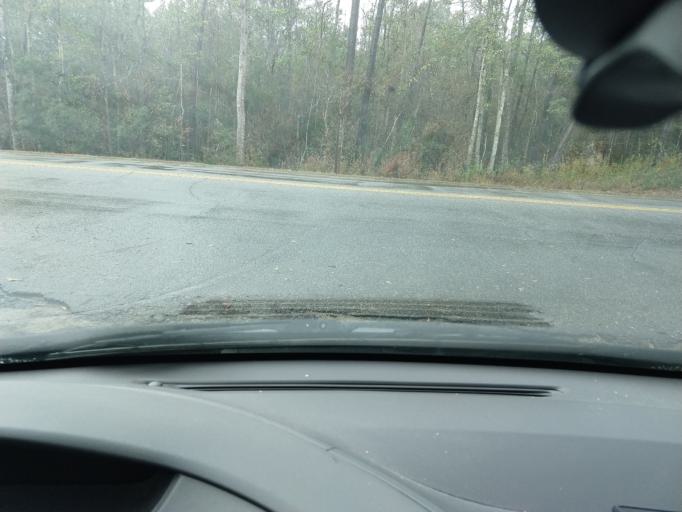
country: US
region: Mississippi
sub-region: Jackson County
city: Gulf Park Estates
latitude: 30.3977
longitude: -88.7573
